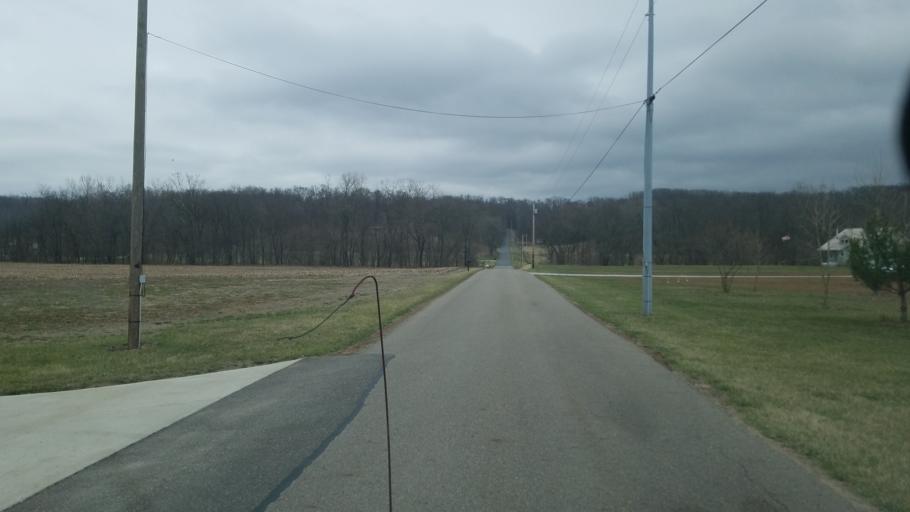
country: US
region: Ohio
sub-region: Licking County
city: Utica
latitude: 40.1988
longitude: -82.4151
